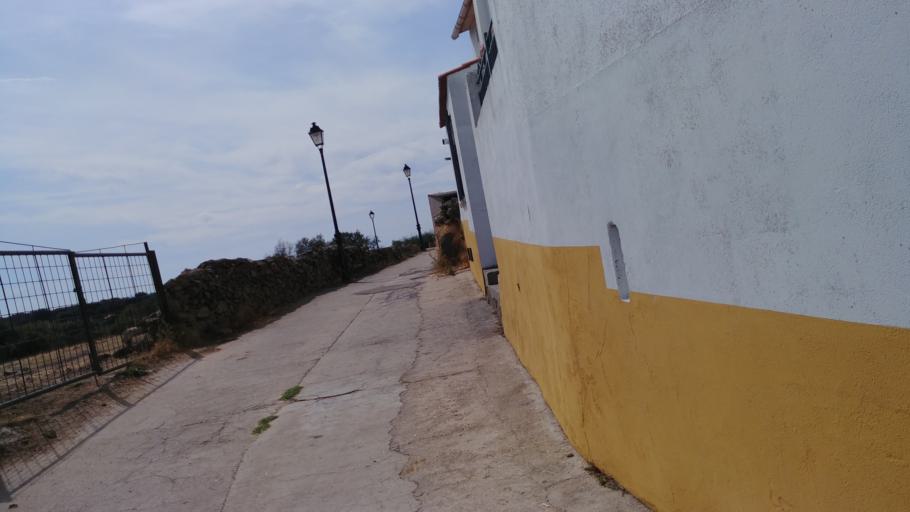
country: ES
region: Castille-La Mancha
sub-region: Province of Toledo
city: Navalcan
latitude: 40.0664
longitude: -5.0956
